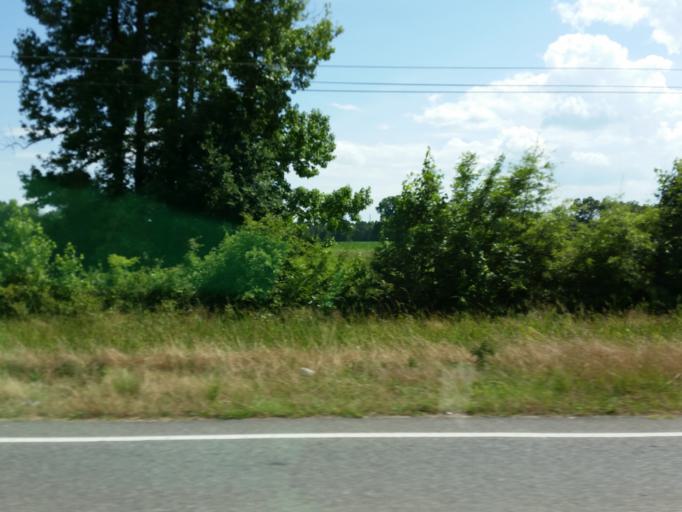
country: US
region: Alabama
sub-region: Marengo County
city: Demopolis
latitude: 32.6392
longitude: -87.8619
